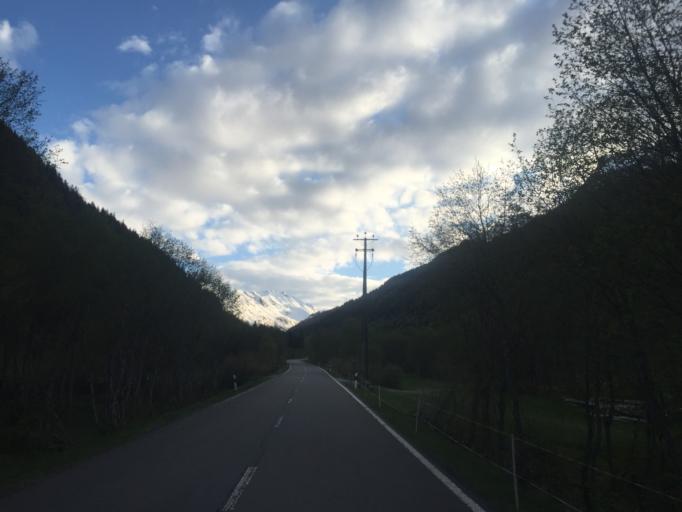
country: CH
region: Ticino
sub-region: Leventina District
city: Airolo
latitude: 46.5080
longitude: 8.5210
